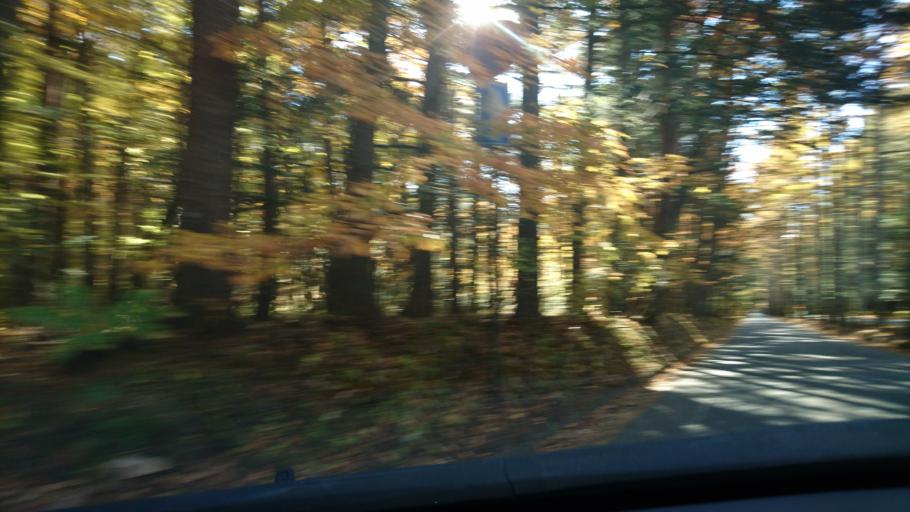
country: JP
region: Nagano
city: Komoro
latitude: 36.3686
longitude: 138.6283
